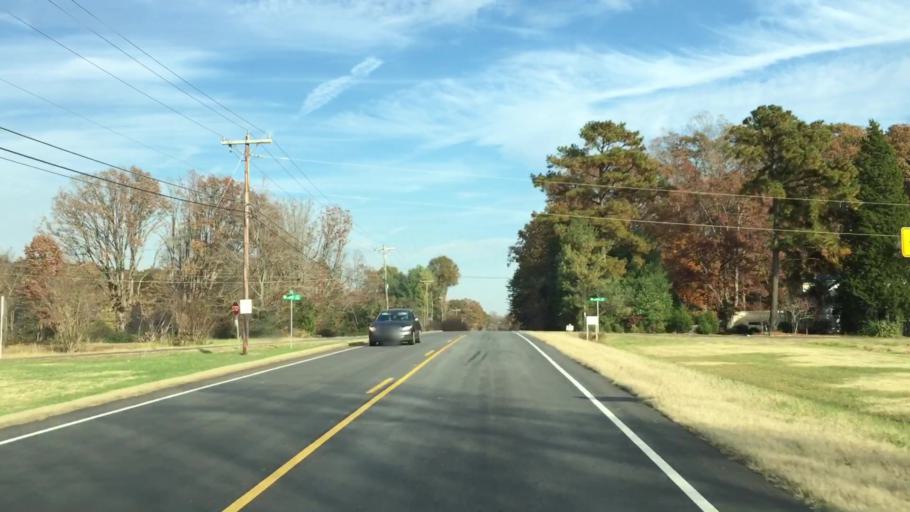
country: US
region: North Carolina
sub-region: Guilford County
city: Summerfield
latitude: 36.2501
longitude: -79.9087
